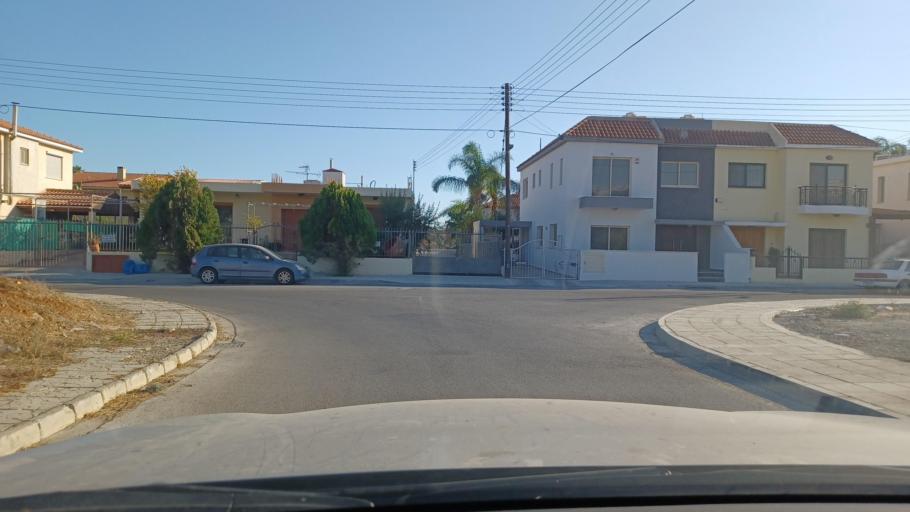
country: CY
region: Limassol
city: Ypsonas
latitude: 34.6607
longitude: 32.9975
